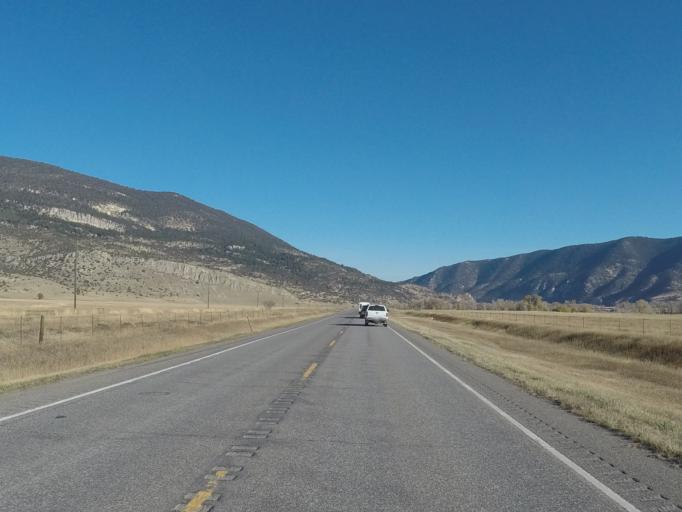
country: US
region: Montana
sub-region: Park County
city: Livingston
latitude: 45.5603
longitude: -110.5934
